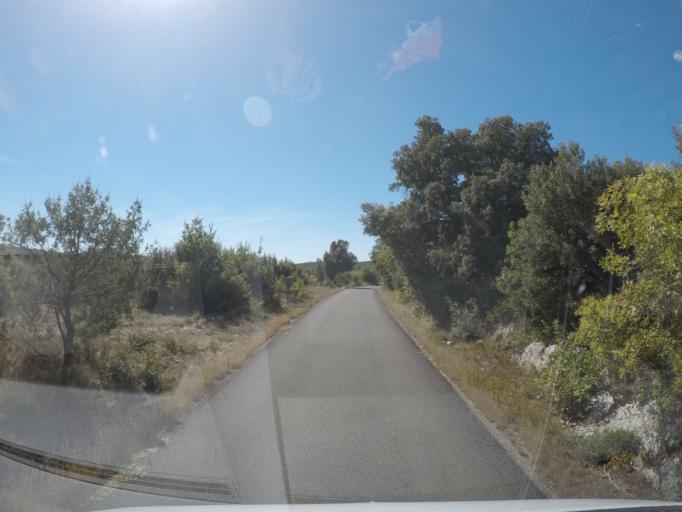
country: FR
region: Languedoc-Roussillon
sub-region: Departement de l'Herault
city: Vailhauques
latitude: 43.7291
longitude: 3.6785
